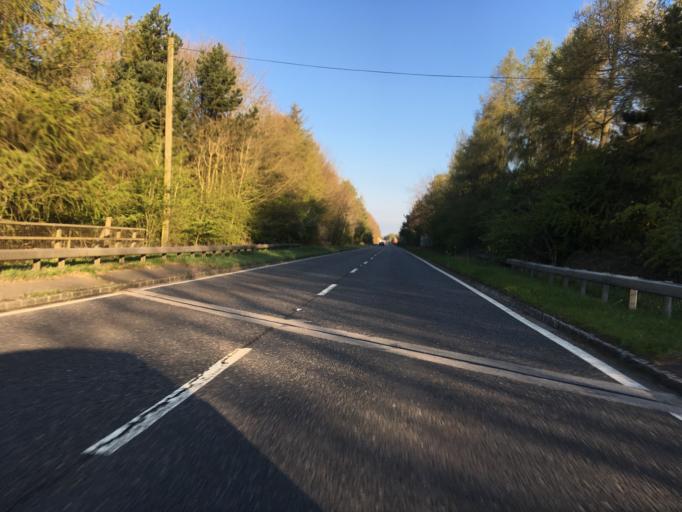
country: GB
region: England
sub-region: Gloucestershire
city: Northleach
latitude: 51.8339
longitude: -1.8249
